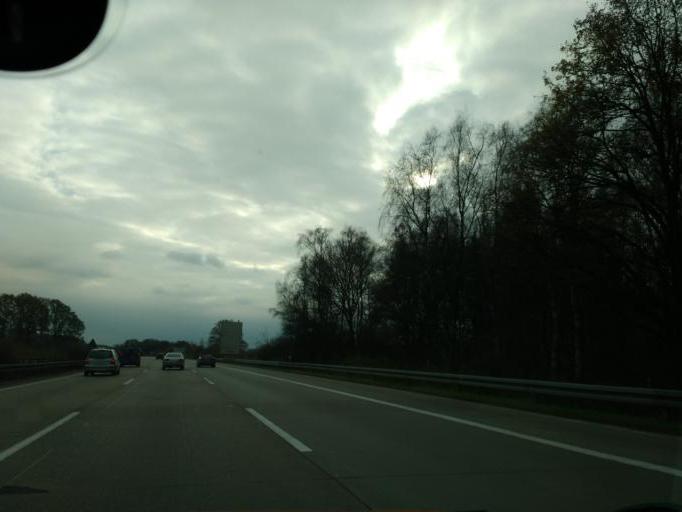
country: DE
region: Lower Saxony
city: Isernhagen Farster Bauerschaft
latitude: 52.4553
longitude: 9.8601
